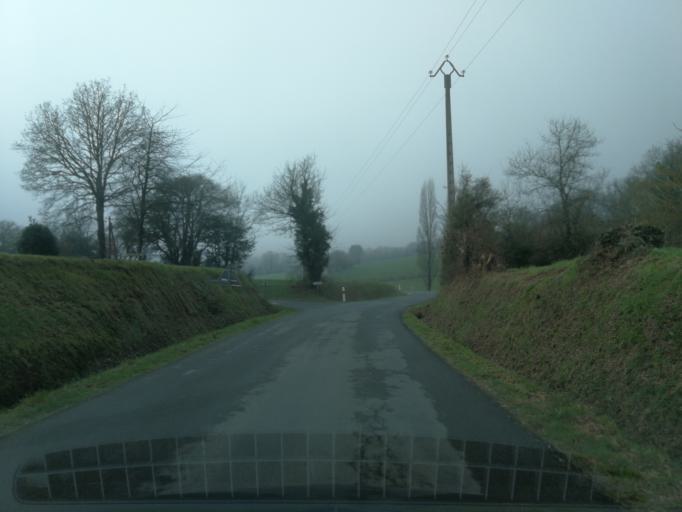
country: FR
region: Brittany
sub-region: Departement du Morbihan
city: La Vraie-Croix
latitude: 47.7347
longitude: -2.5056
